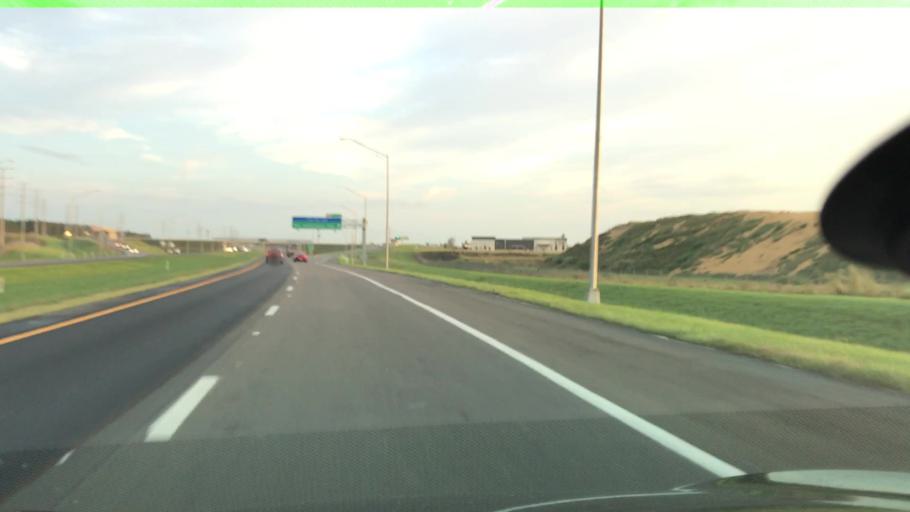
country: US
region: Florida
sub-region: Orange County
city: Oakland
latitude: 28.4674
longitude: -81.6314
